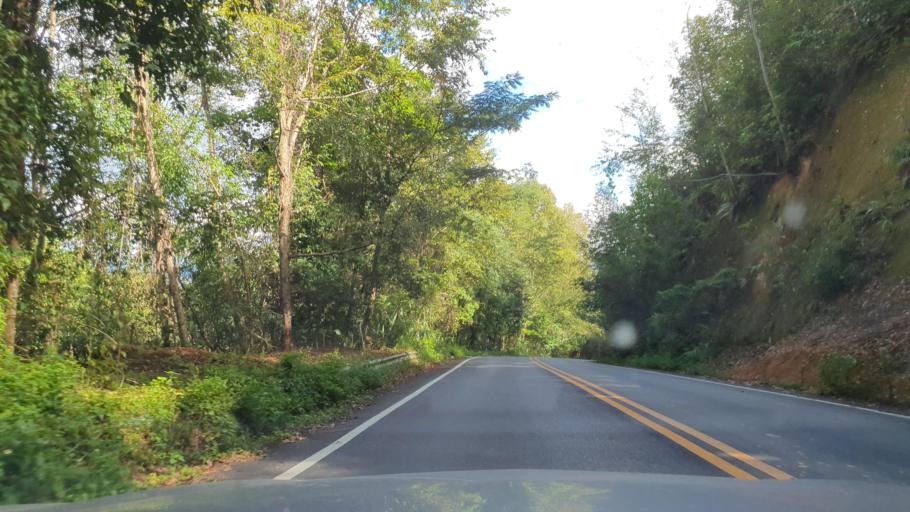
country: TH
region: Chiang Rai
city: Wiang Pa Pao
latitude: 19.3034
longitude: 99.3614
